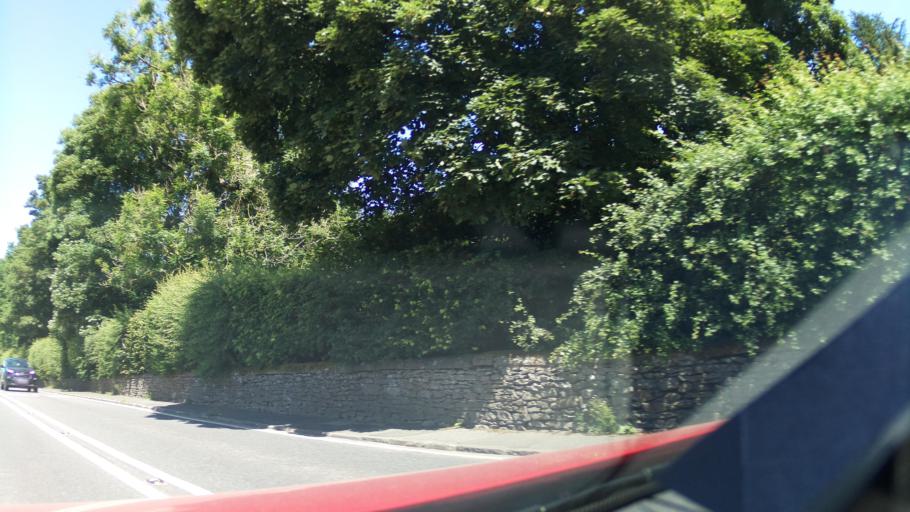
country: GB
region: England
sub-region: Derbyshire
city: Bakewell
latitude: 53.1927
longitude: -1.6528
